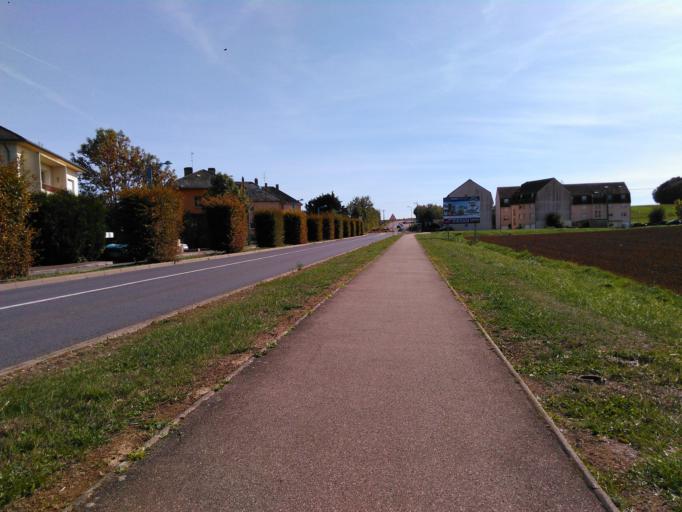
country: FR
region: Lorraine
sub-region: Departement de la Moselle
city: Hettange-Grande
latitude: 49.3951
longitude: 6.1649
